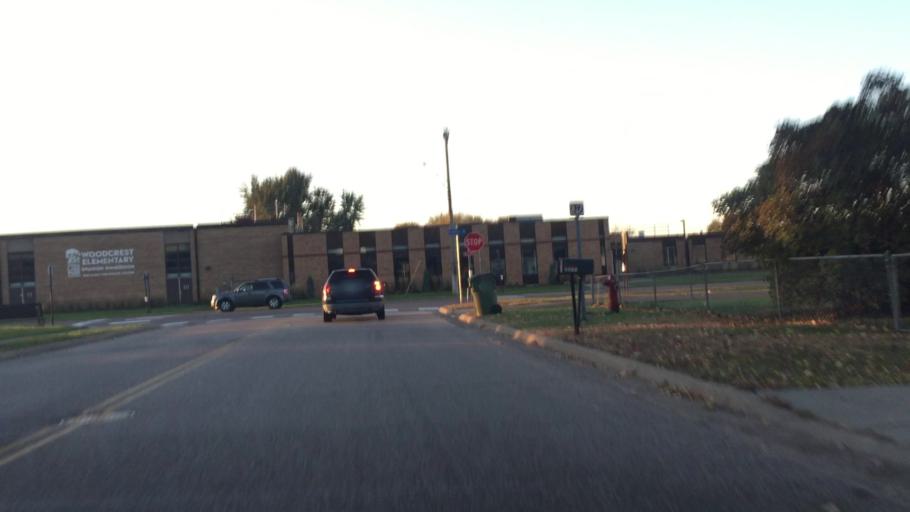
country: US
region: Minnesota
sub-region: Anoka County
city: Spring Lake Park
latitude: 45.1083
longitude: -93.2484
